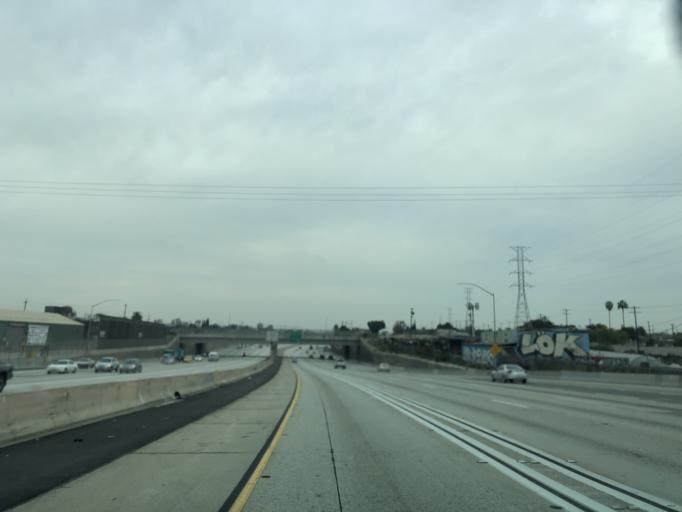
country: US
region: California
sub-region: Los Angeles County
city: West Rancho Dominguez
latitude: 33.8940
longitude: -118.2857
